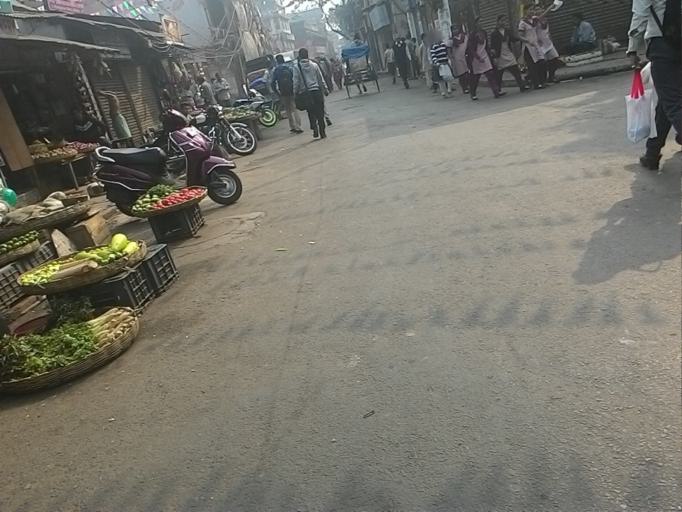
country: IN
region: West Bengal
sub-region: Kolkata
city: Bara Bazar
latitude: 22.5331
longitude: 88.3467
